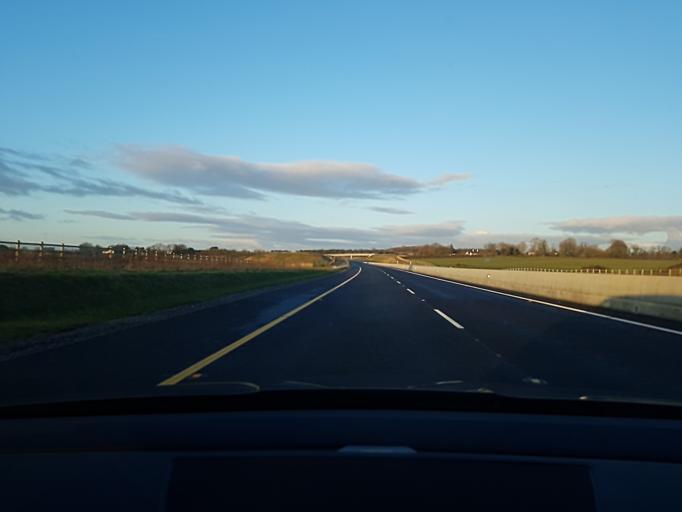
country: IE
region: Connaught
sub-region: County Galway
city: Athenry
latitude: 53.3556
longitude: -8.7940
